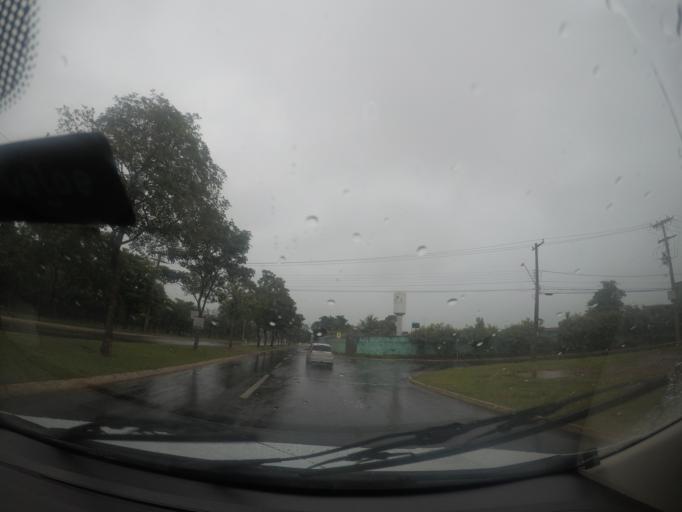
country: BR
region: Goias
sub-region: Goiania
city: Goiania
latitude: -16.6000
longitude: -49.3305
